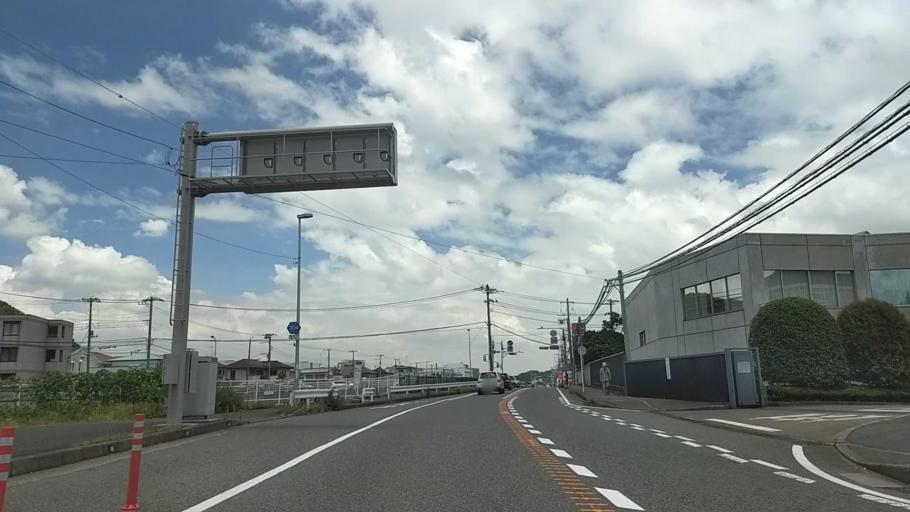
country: JP
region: Kanagawa
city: Fujisawa
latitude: 35.3330
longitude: 139.5097
